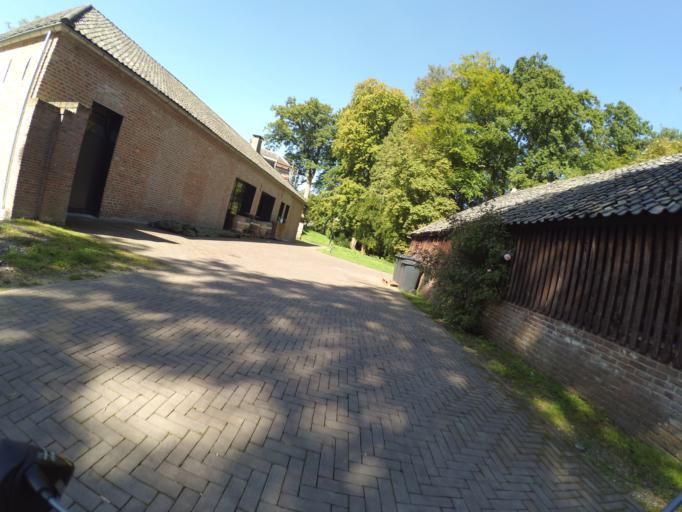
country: NL
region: Utrecht
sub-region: Gemeente Utrechtse Heuvelrug
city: Leersum
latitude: 52.0080
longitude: 5.4022
